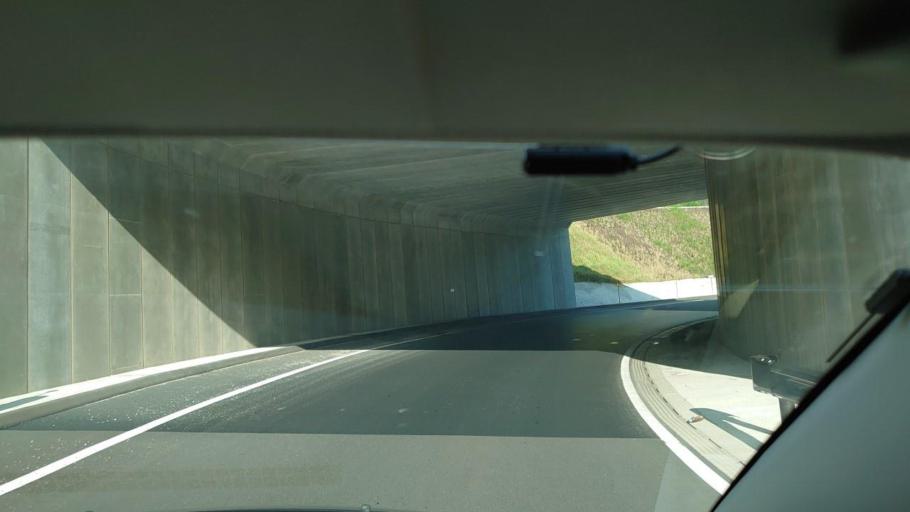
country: JP
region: Iwate
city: Ofunato
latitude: 38.8981
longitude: 141.5950
